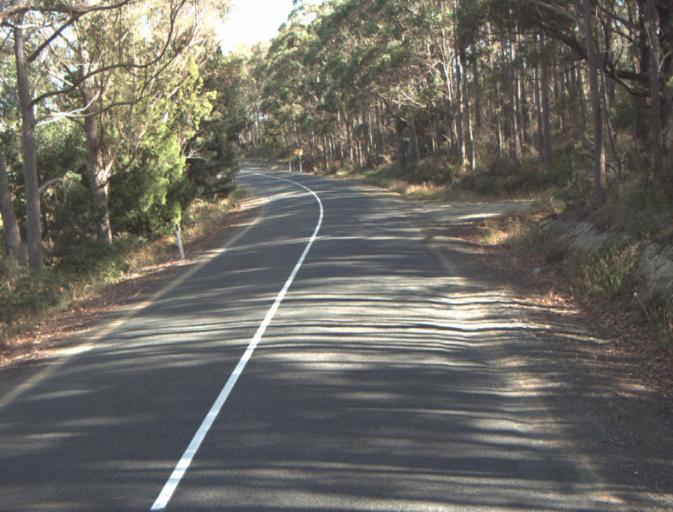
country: AU
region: Tasmania
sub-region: Dorset
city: Bridport
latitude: -41.1471
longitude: 147.2327
